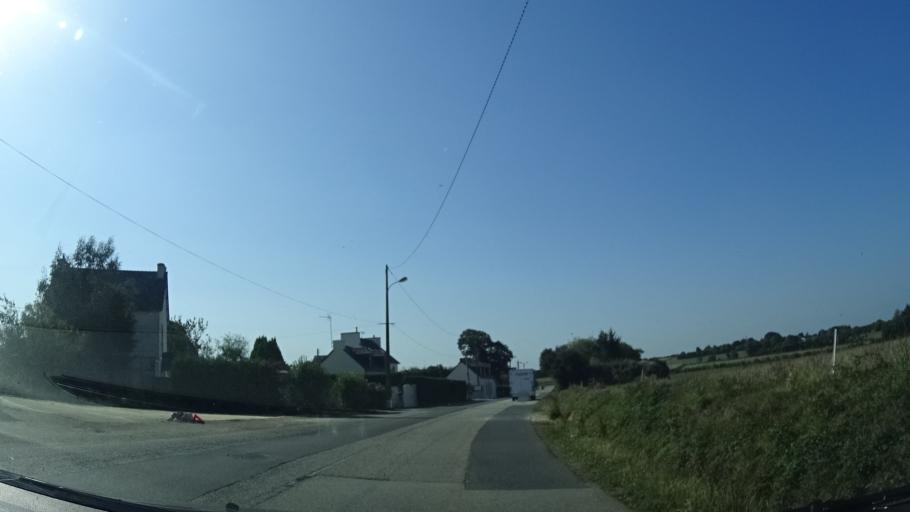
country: FR
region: Brittany
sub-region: Departement du Finistere
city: Cast
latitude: 48.1527
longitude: -4.1419
